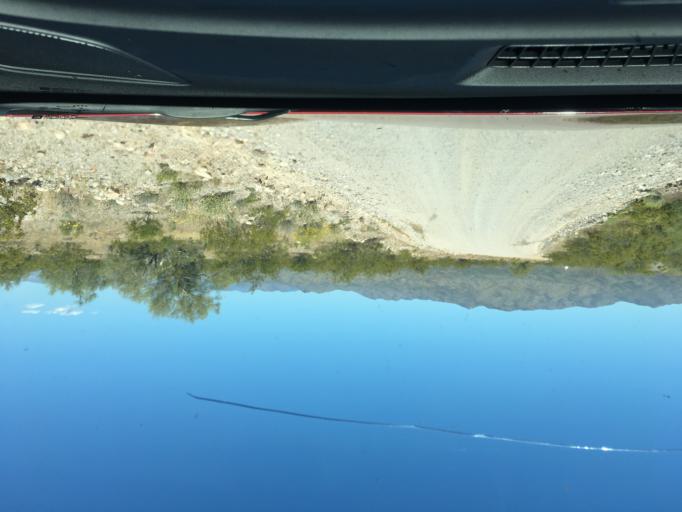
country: US
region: Arizona
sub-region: Yavapai County
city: Bagdad
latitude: 34.6113
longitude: -113.5186
